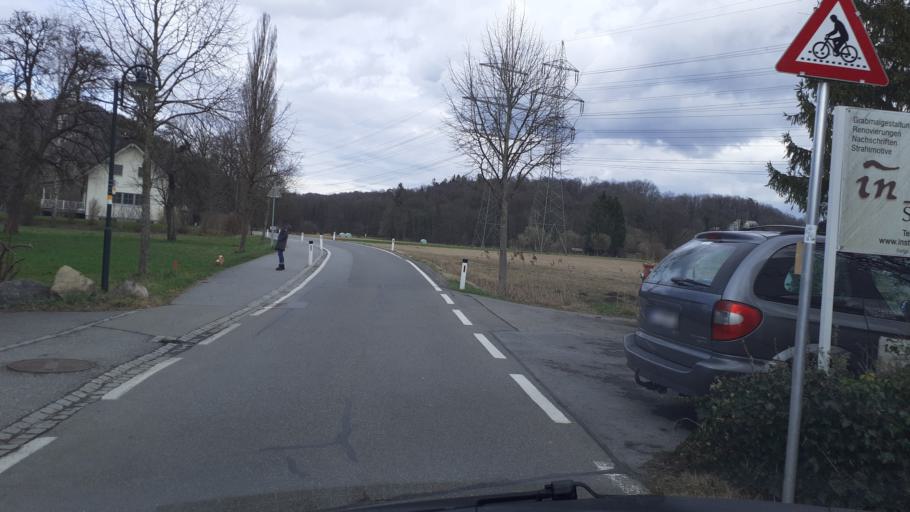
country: AT
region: Vorarlberg
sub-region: Politischer Bezirk Feldkirch
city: Koblach
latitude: 47.3179
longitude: 9.6158
